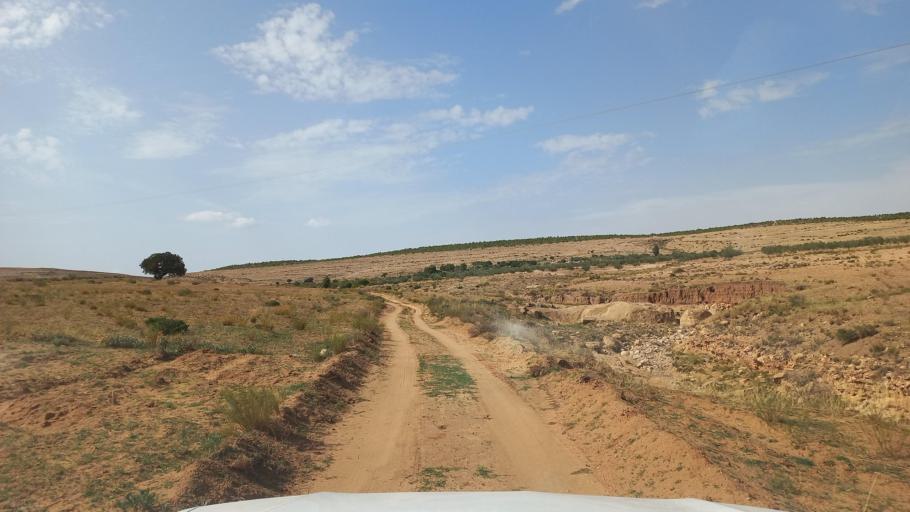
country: TN
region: Al Qasrayn
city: Kasserine
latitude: 35.3628
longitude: 8.8600
